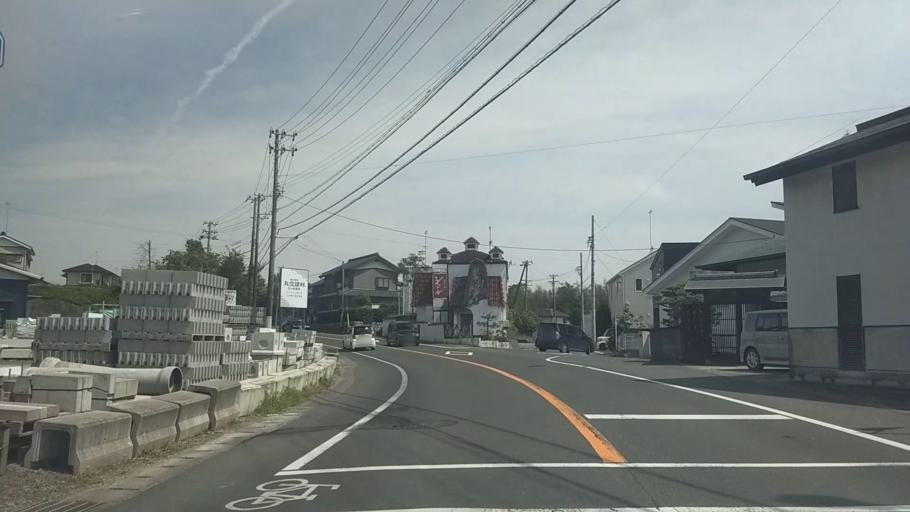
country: JP
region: Shizuoka
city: Kosai-shi
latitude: 34.7959
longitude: 137.5718
